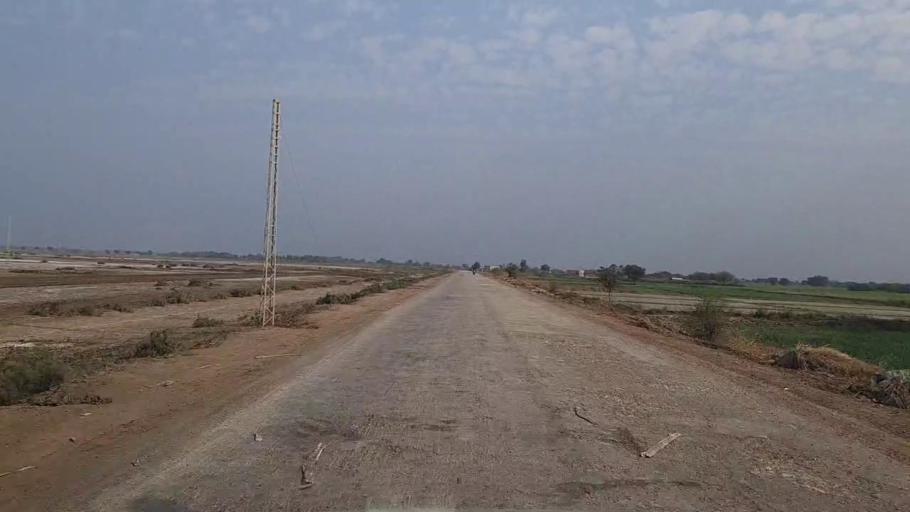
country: PK
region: Sindh
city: Mirwah Gorchani
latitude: 25.4070
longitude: 69.0447
